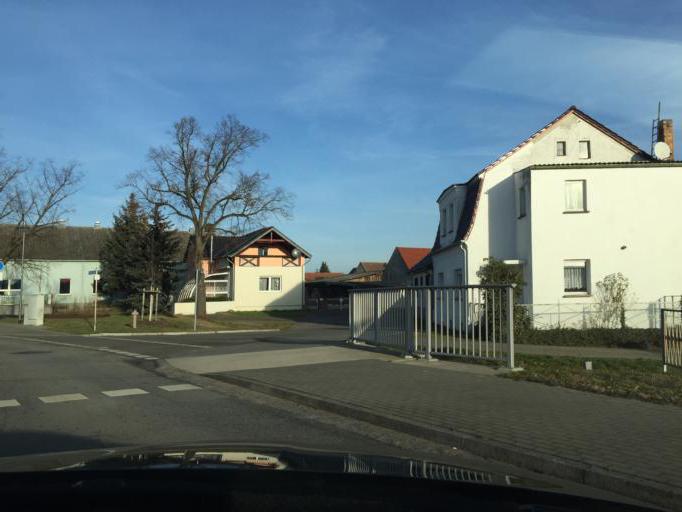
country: DE
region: Brandenburg
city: Ziltendorf
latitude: 52.2040
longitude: 14.6278
